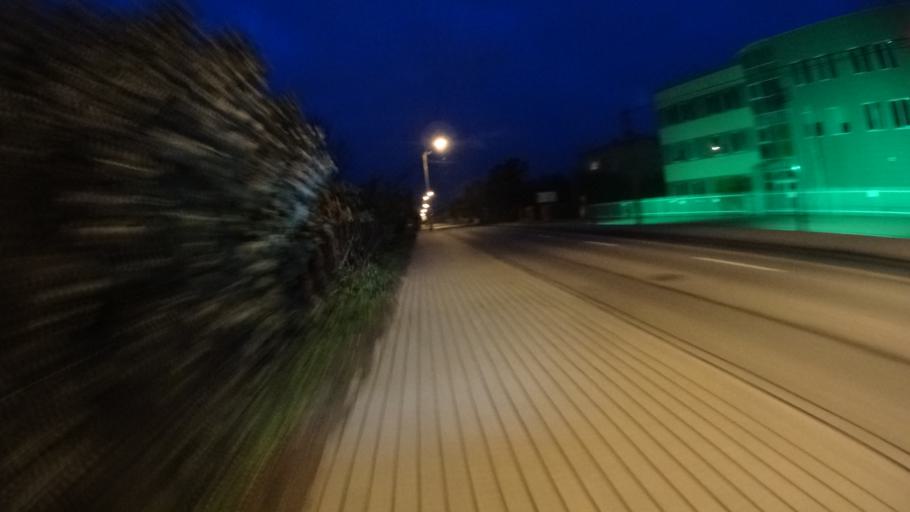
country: PL
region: Masovian Voivodeship
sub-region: Powiat warszawski zachodni
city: Babice
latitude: 52.2285
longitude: 20.8439
